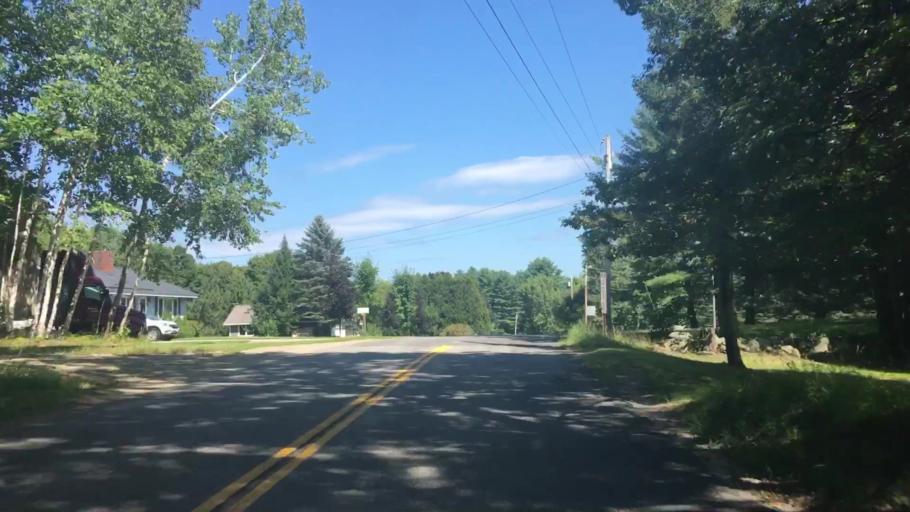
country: US
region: Maine
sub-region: Androscoggin County
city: Lisbon
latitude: 44.0639
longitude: -70.1165
